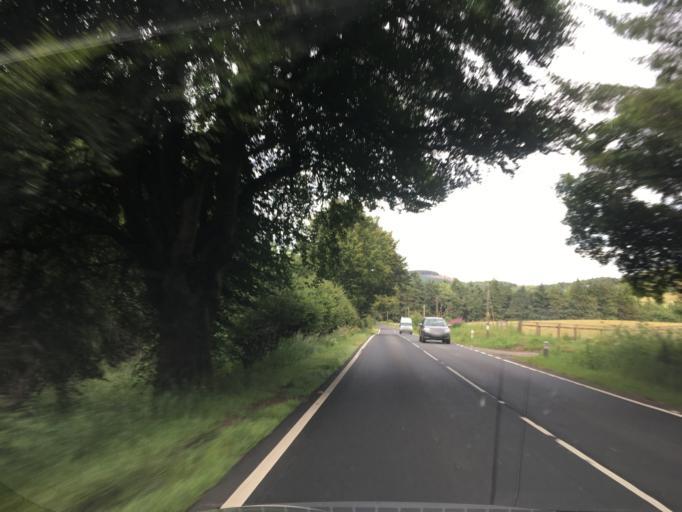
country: GB
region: Scotland
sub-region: South Lanarkshire
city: Biggar
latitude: 55.5784
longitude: -3.5745
